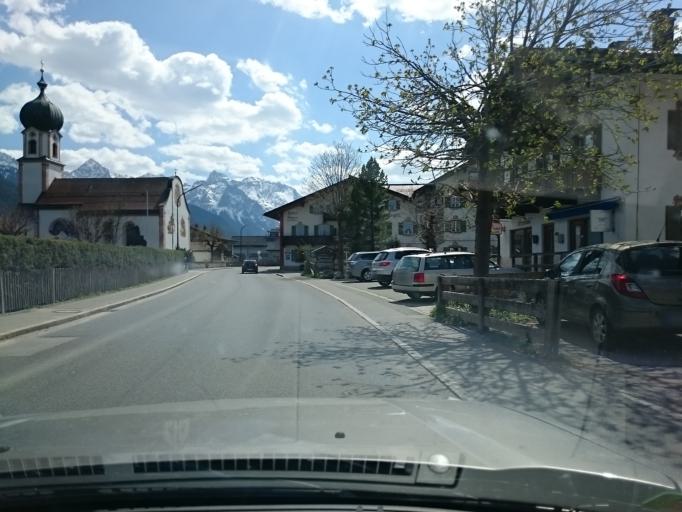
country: DE
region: Bavaria
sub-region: Upper Bavaria
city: Krun
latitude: 47.5046
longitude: 11.2785
